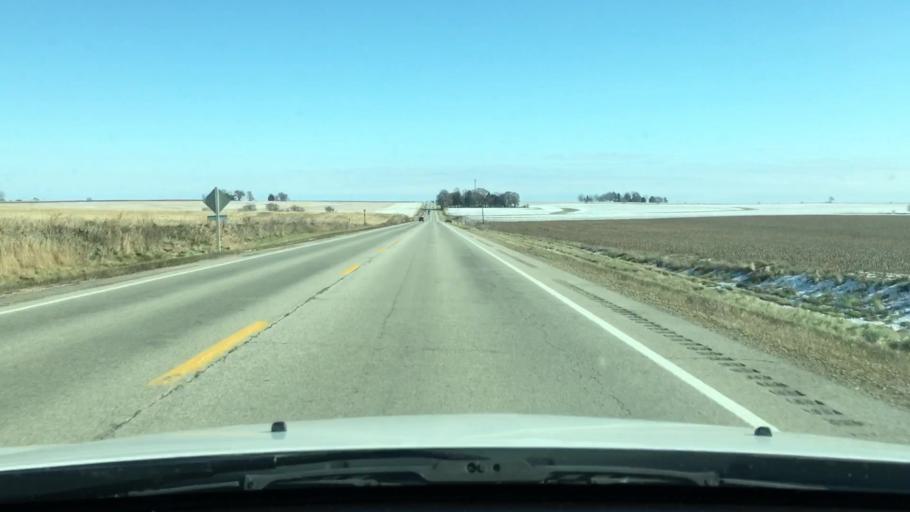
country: US
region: Illinois
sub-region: DeKalb County
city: Malta
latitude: 42.0010
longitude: -88.8957
